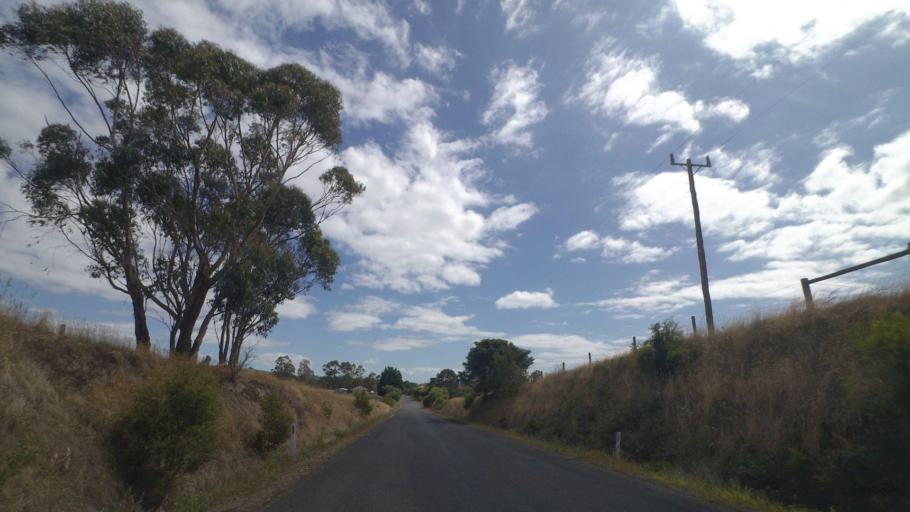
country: AU
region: Victoria
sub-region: Cardinia
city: Bunyip
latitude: -38.3090
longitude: 145.7584
